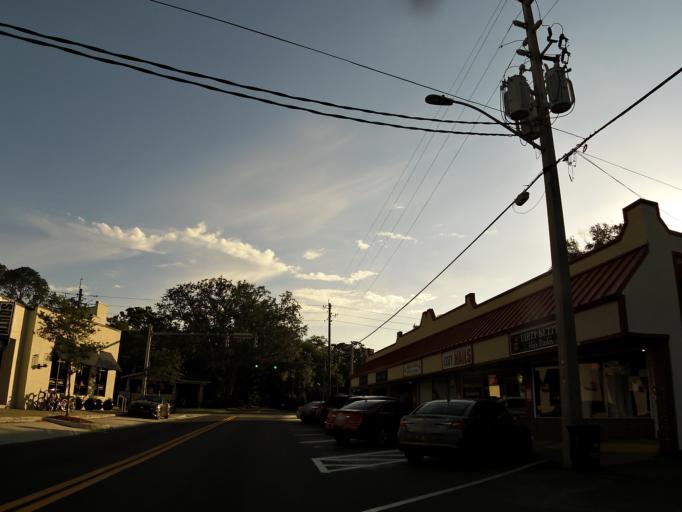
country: US
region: Florida
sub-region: Duval County
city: Jacksonville
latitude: 30.3004
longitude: -81.7102
